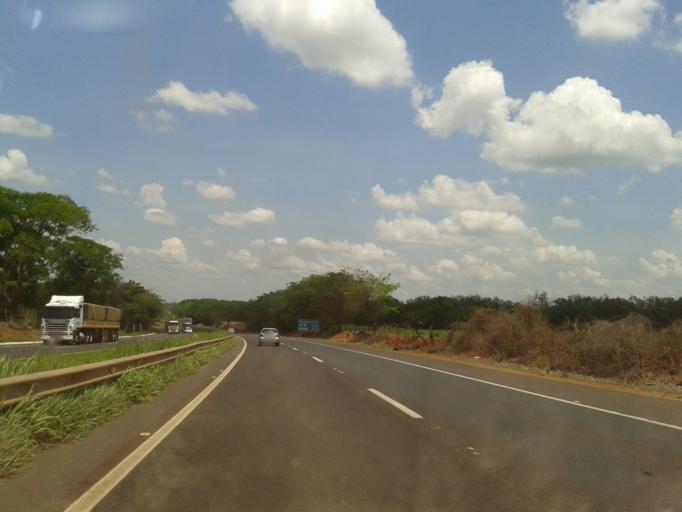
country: BR
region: Minas Gerais
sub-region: Monte Alegre De Minas
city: Monte Alegre de Minas
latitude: -18.8666
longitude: -48.5936
